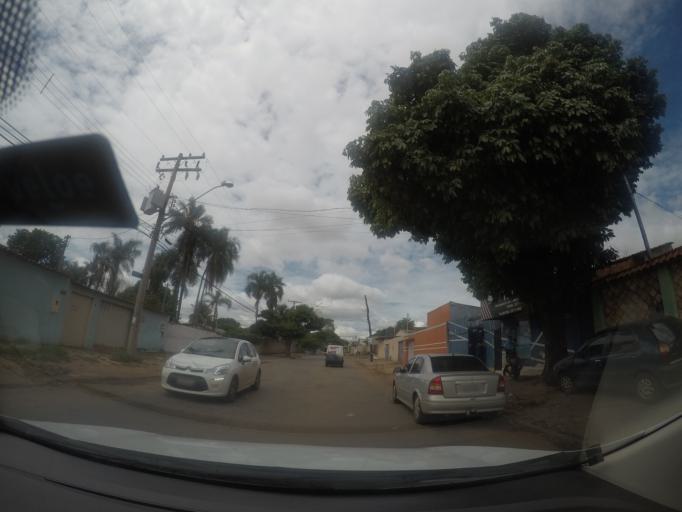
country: BR
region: Goias
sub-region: Goiania
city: Goiania
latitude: -16.6582
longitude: -49.2967
